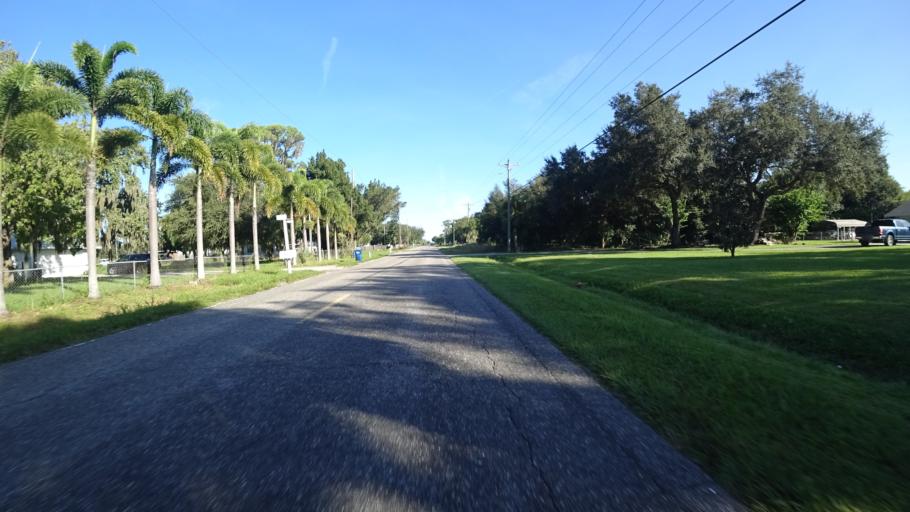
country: US
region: Florida
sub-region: Manatee County
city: Memphis
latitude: 27.5919
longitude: -82.5272
